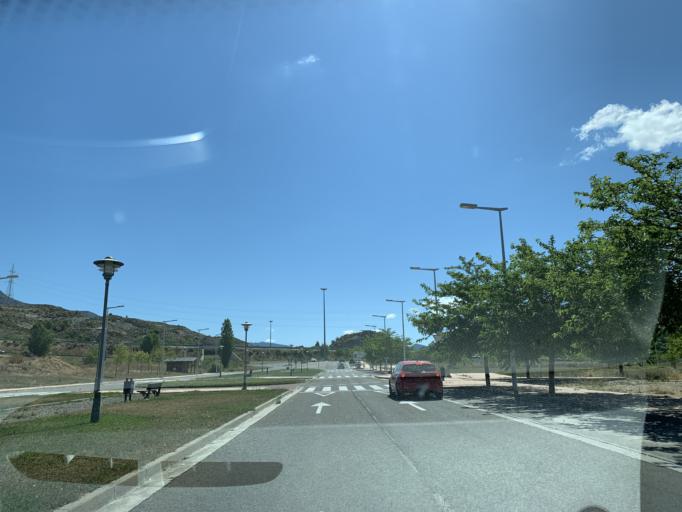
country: ES
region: Aragon
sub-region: Provincia de Huesca
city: Sabinanigo
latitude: 42.5048
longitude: -0.3564
